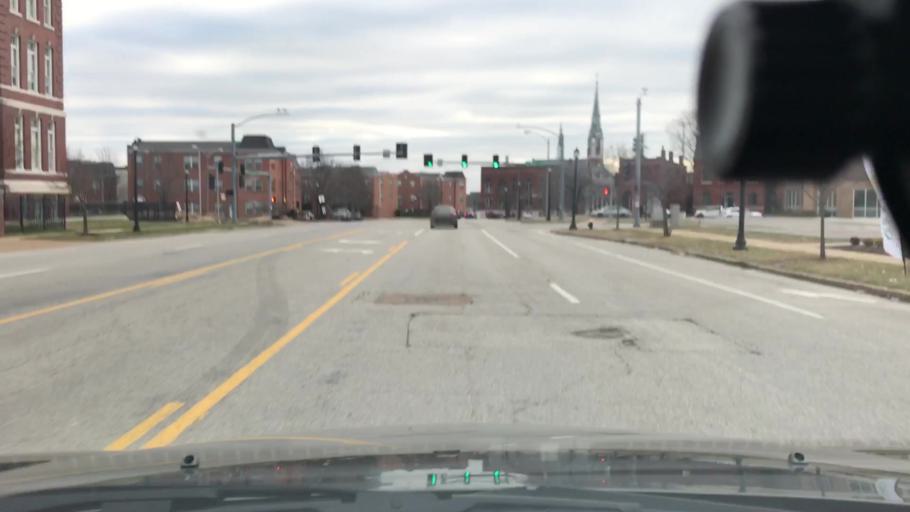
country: US
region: Missouri
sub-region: City of Saint Louis
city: St. Louis
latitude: 38.6133
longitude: -90.2087
